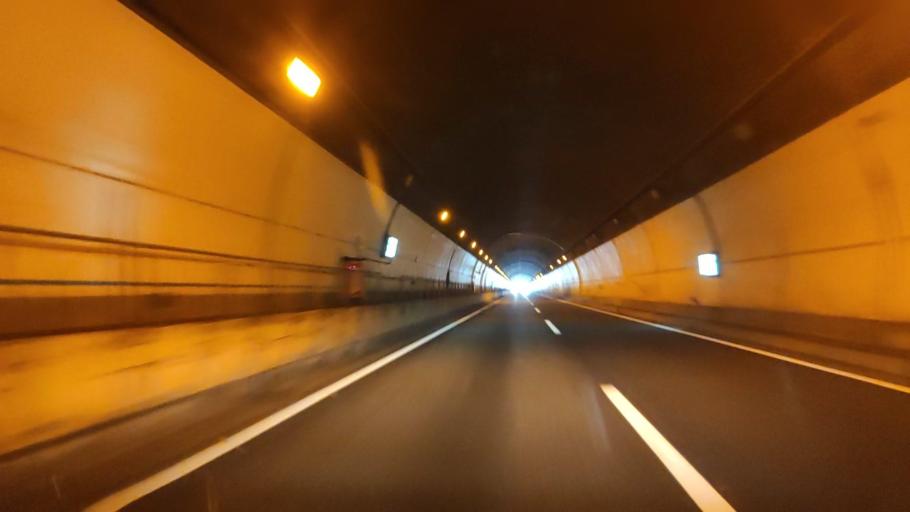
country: JP
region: Akita
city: Hanawa
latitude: 40.0157
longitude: 140.9862
